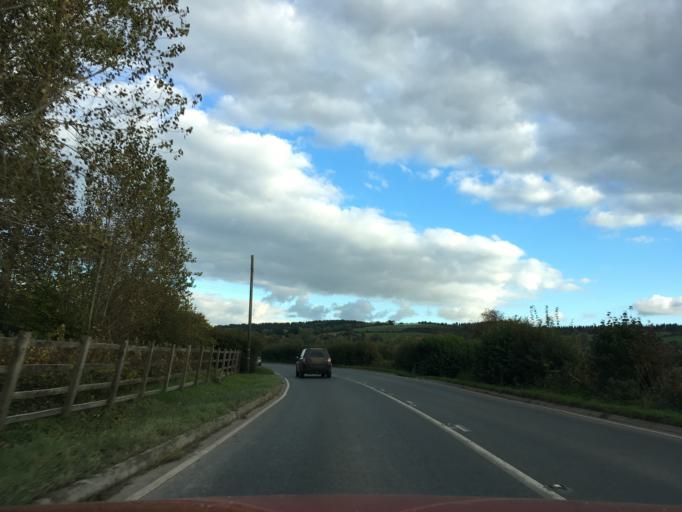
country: GB
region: England
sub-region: Herefordshire
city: Withington
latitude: 52.0596
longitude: -2.6196
